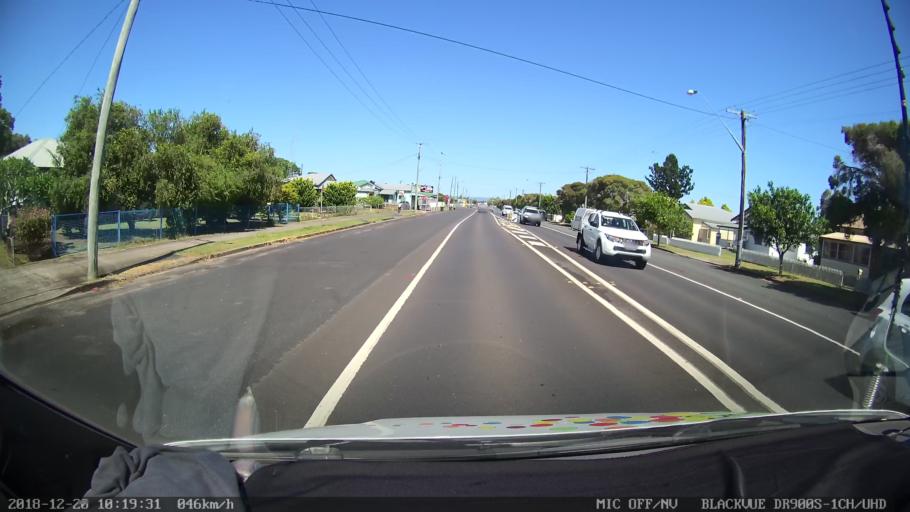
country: AU
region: New South Wales
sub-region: Richmond Valley
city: Casino
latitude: -28.8595
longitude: 153.0535
